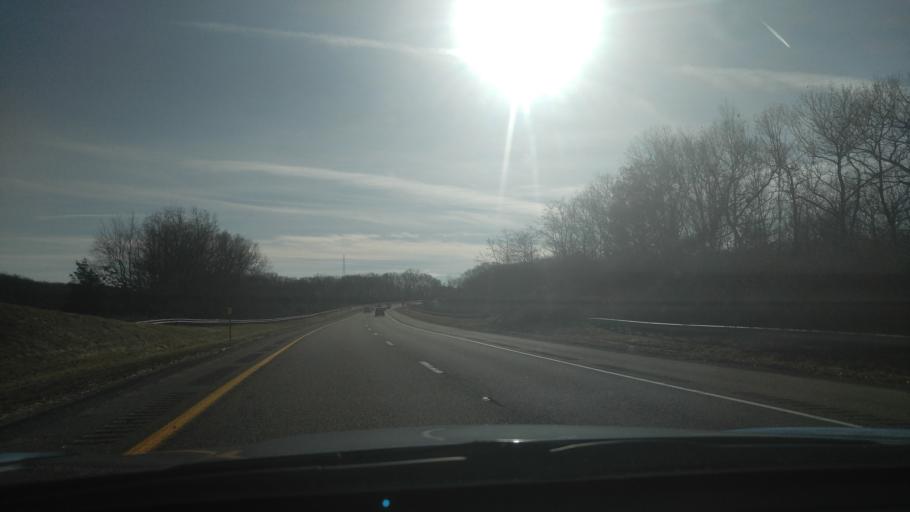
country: US
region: Rhode Island
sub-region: Providence County
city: Cumberland Hill
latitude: 41.9564
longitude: -71.4831
